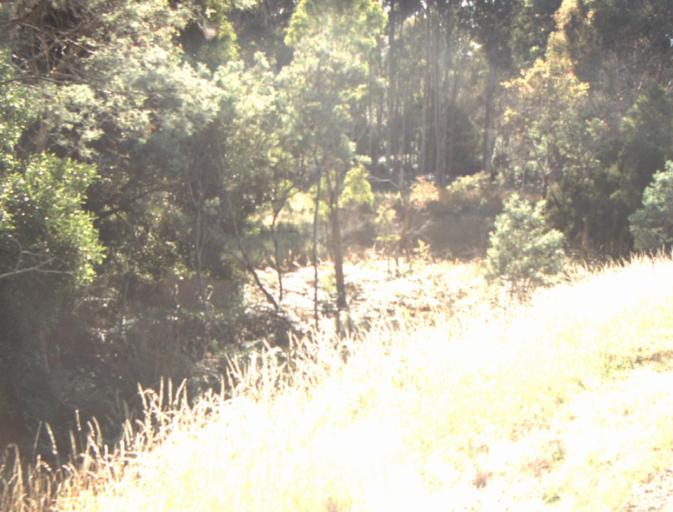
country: AU
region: Tasmania
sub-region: Launceston
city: Newstead
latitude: -41.4185
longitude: 147.2633
